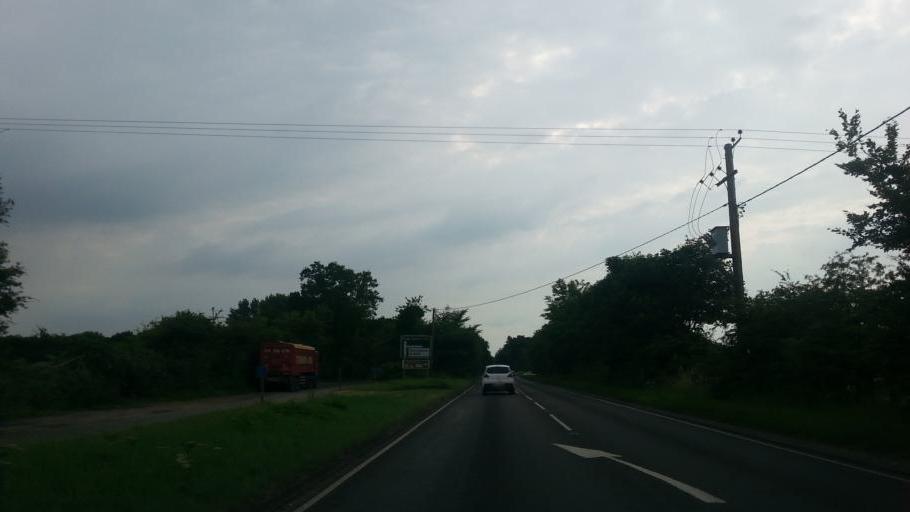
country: GB
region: England
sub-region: Norfolk
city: Dersingham
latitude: 52.7993
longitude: 0.5394
